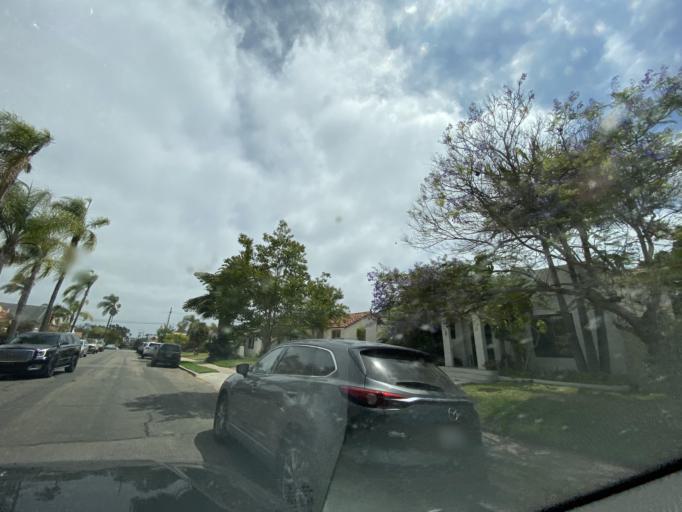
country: US
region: California
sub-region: San Diego County
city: San Diego
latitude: 32.7365
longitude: -117.1231
